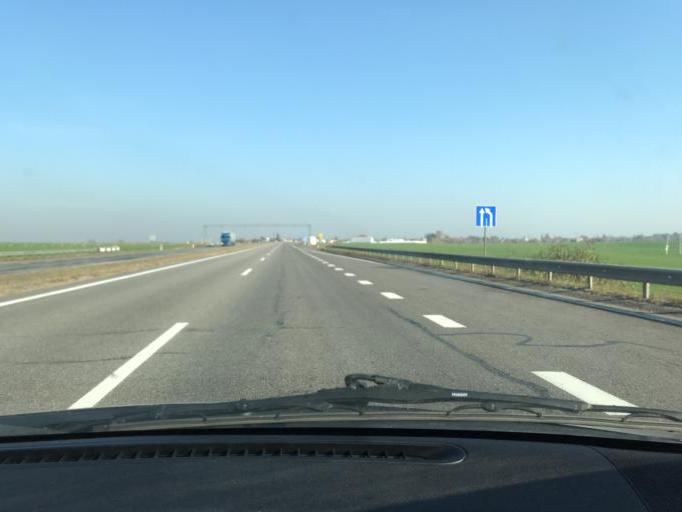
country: BY
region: Vitebsk
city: Horad Orsha
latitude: 54.5960
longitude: 30.3500
